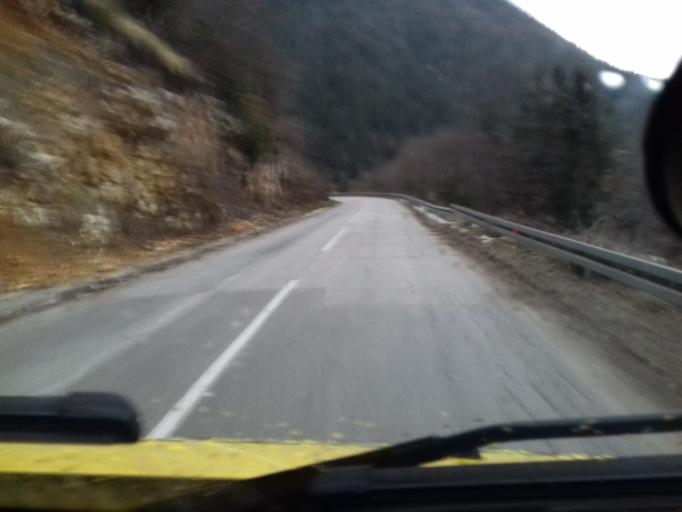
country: BA
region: Federation of Bosnia and Herzegovina
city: Turbe
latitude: 44.2852
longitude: 17.5029
